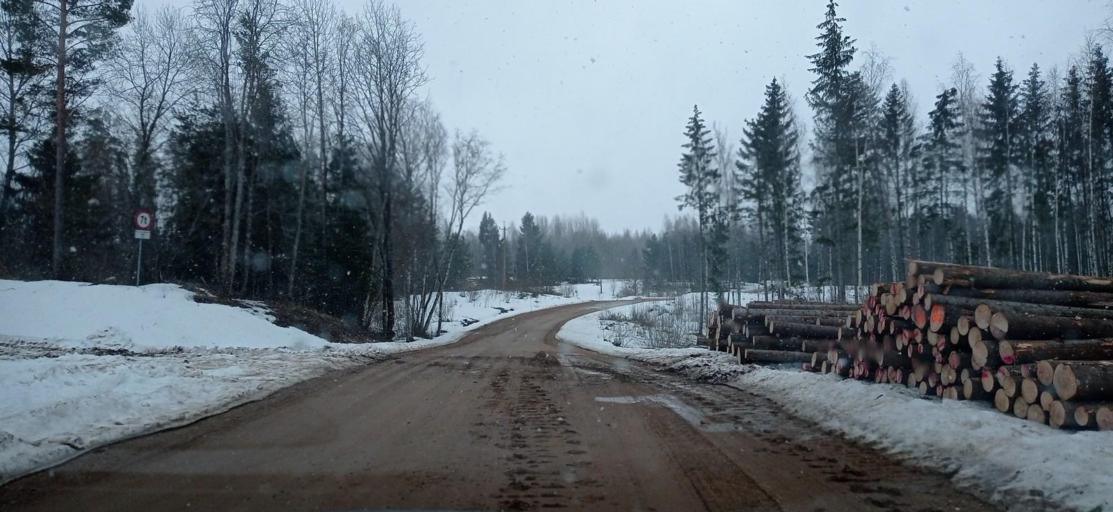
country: EE
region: Tartu
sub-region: UElenurme vald
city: Ulenurme
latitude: 58.1174
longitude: 26.7001
